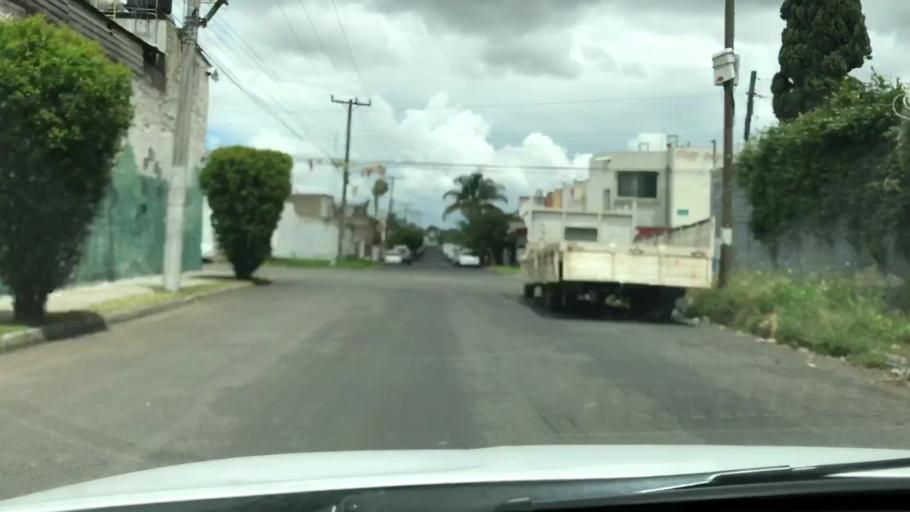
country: MX
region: Jalisco
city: Guadalajara
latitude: 20.6434
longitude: -103.4378
